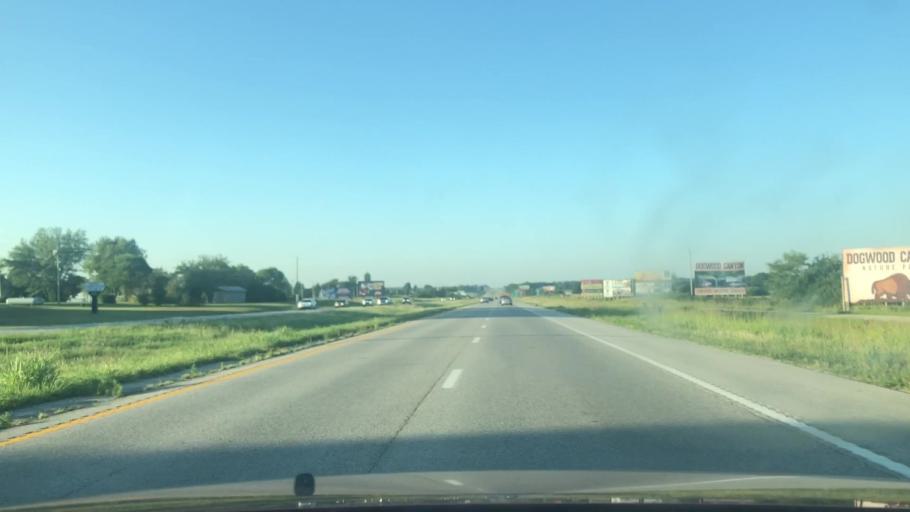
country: US
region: Missouri
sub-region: Christian County
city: Ozark
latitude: 36.9684
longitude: -93.2316
